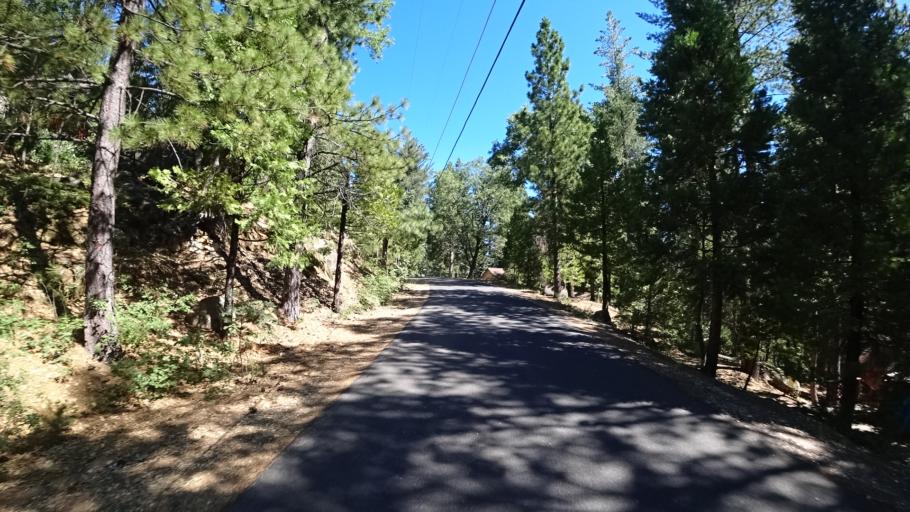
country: US
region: California
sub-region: Calaveras County
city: Arnold
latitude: 38.2873
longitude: -120.2761
